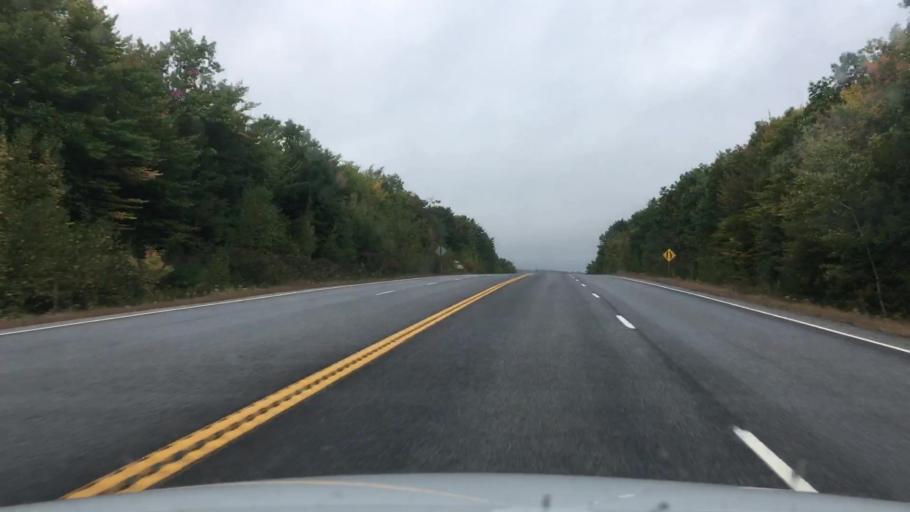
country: US
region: Maine
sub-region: Cumberland County
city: New Gloucester
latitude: 43.9585
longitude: -70.3547
